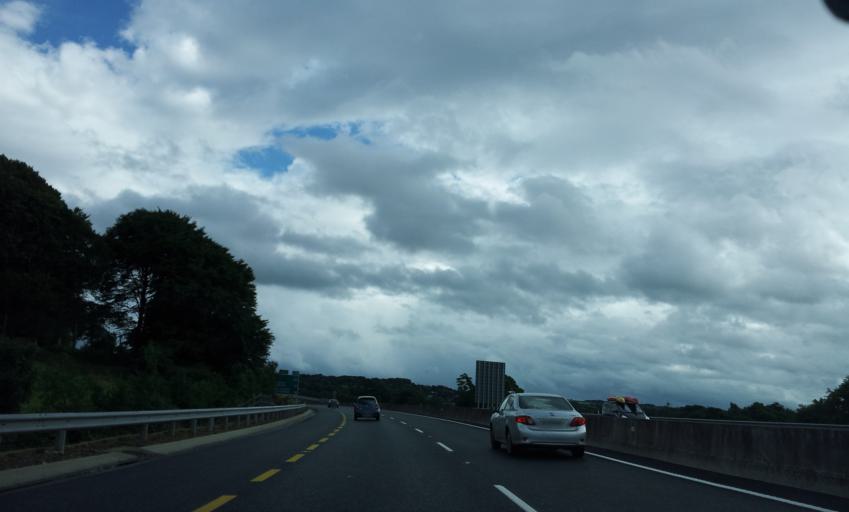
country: IE
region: Leinster
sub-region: Kilkenny
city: Mooncoin
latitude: 52.2487
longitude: -7.1908
